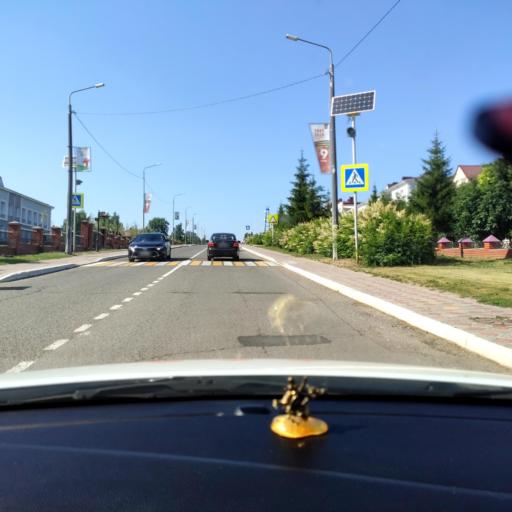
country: RU
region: Tatarstan
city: Laishevo
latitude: 55.4025
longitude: 49.5436
